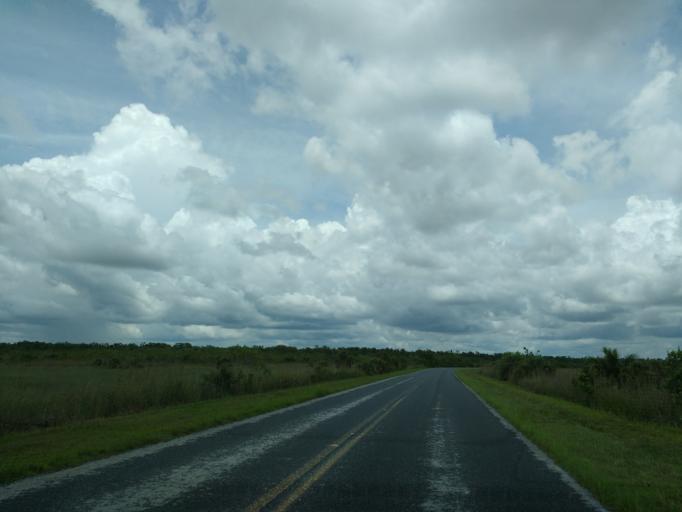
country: US
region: Florida
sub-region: Miami-Dade County
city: Florida City
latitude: 25.3891
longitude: -80.6141
